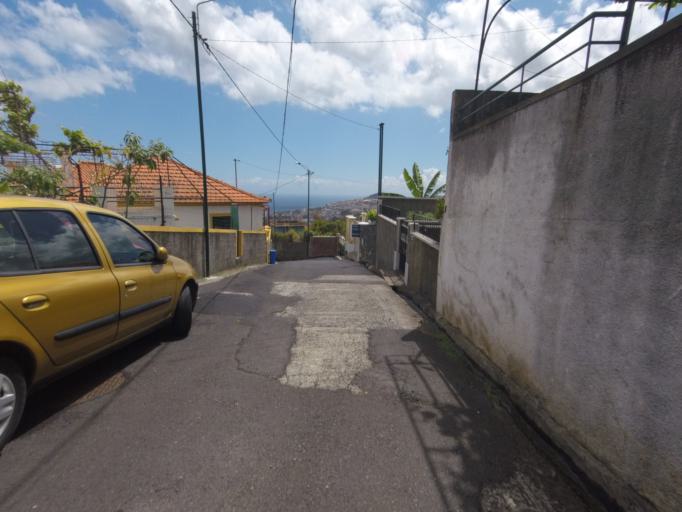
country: PT
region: Madeira
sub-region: Funchal
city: Nossa Senhora do Monte
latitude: 32.6640
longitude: -16.9086
